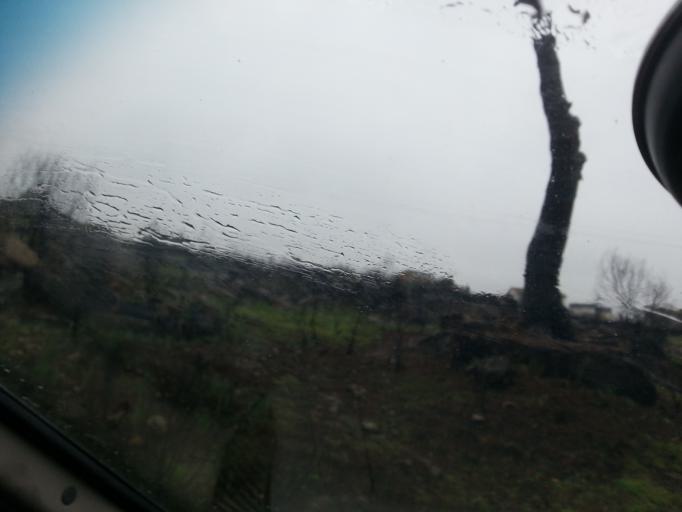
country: PT
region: Viseu
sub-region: Mangualde
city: Mangualde
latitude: 40.6136
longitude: -7.7856
